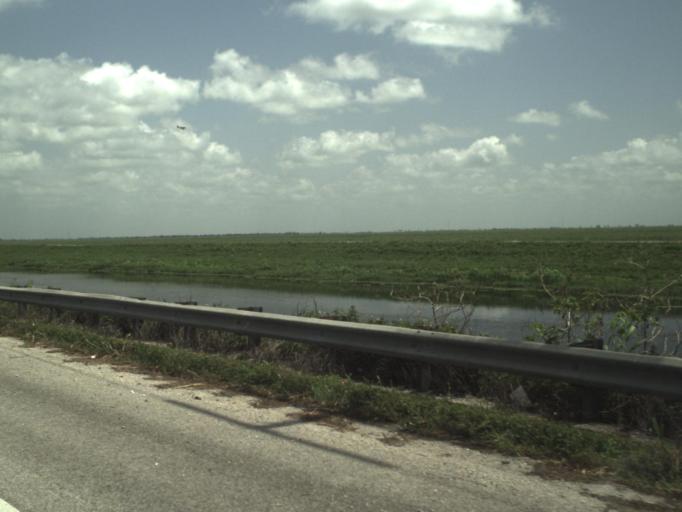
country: US
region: Florida
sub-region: Palm Beach County
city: South Bay
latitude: 26.6106
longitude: -80.7115
